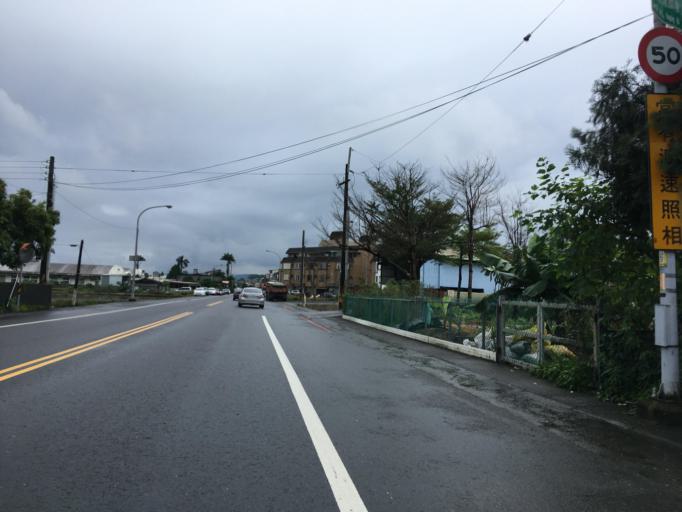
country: TW
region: Taiwan
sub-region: Yilan
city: Yilan
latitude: 24.6583
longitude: 121.7576
